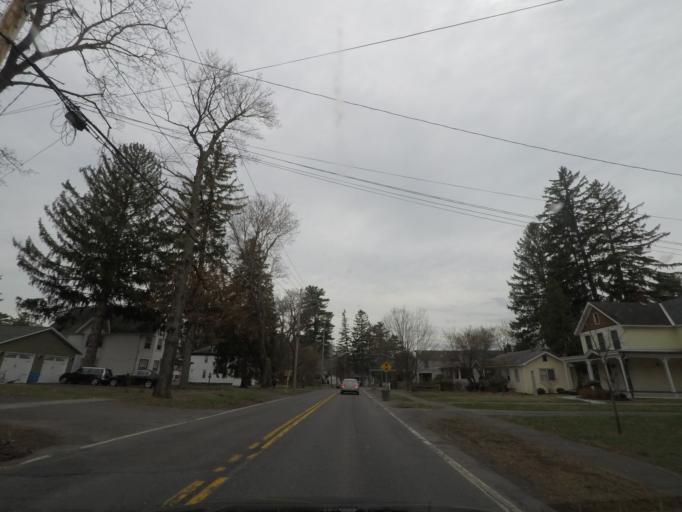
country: US
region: New York
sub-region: Albany County
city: Delmar
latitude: 42.6229
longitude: -73.8205
